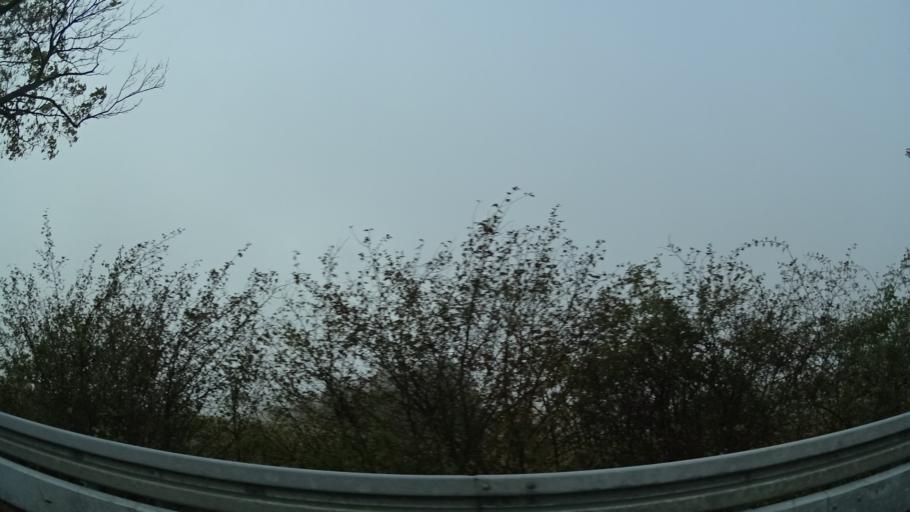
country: DE
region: Hesse
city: Gedern
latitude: 50.4422
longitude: 9.2095
